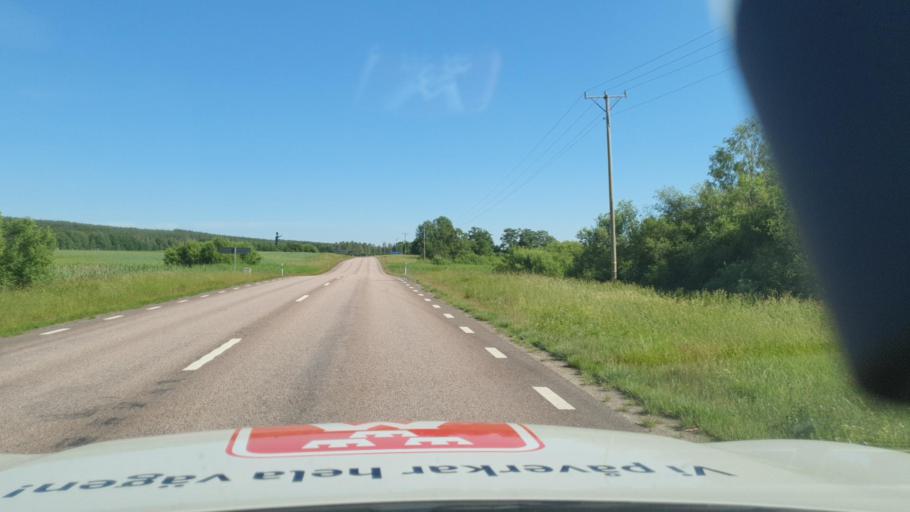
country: SE
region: OErebro
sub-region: Karlskoga Kommun
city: Karlskoga
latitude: 59.4389
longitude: 14.4060
